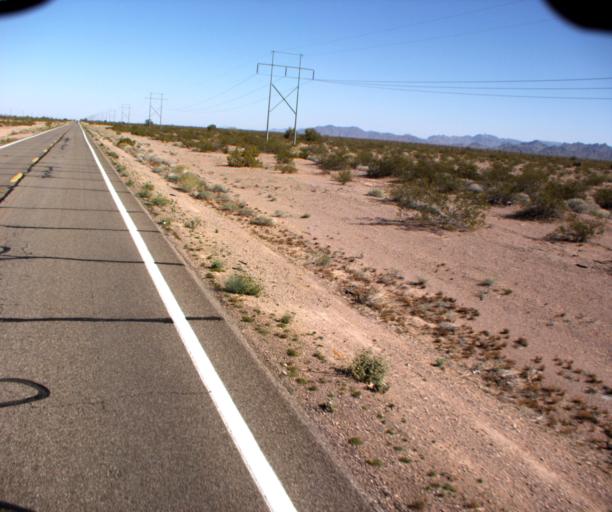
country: US
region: Arizona
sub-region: La Paz County
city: Quartzsite
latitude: 33.4225
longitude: -114.2170
